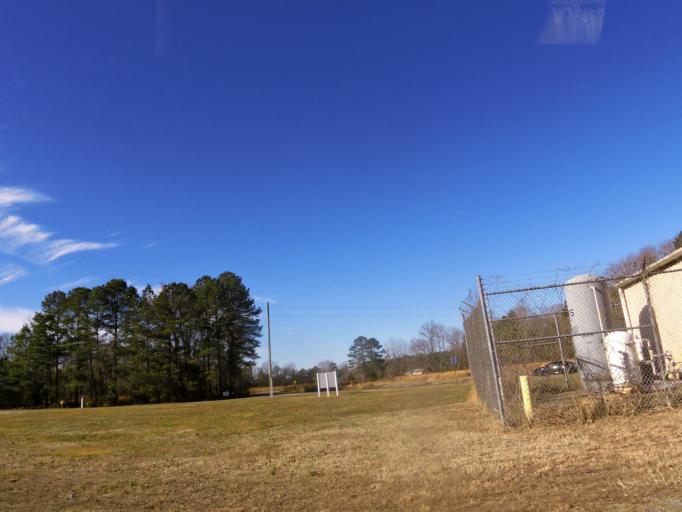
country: US
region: Virginia
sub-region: City of Petersburg
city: Petersburg
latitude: 37.1794
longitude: -77.4214
